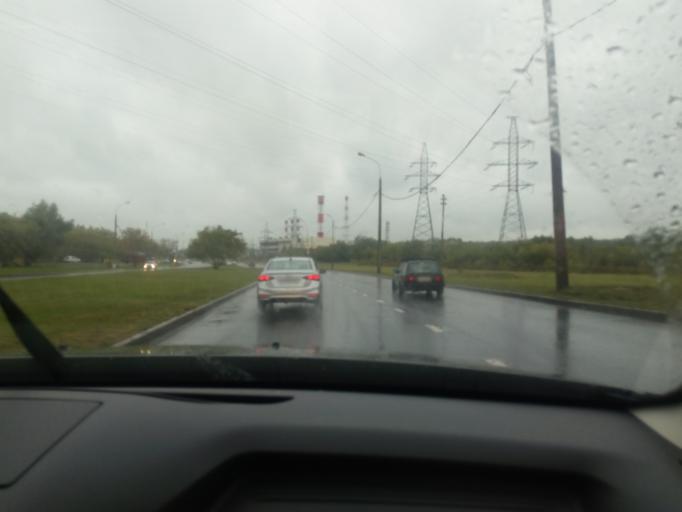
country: RU
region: Moscow
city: Zhulebino
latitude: 55.7172
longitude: 37.8760
